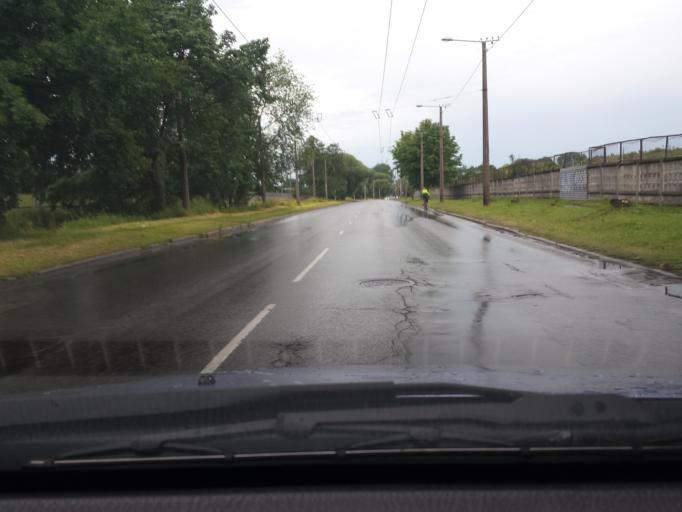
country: LV
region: Riga
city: Riga
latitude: 56.9254
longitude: 24.1770
